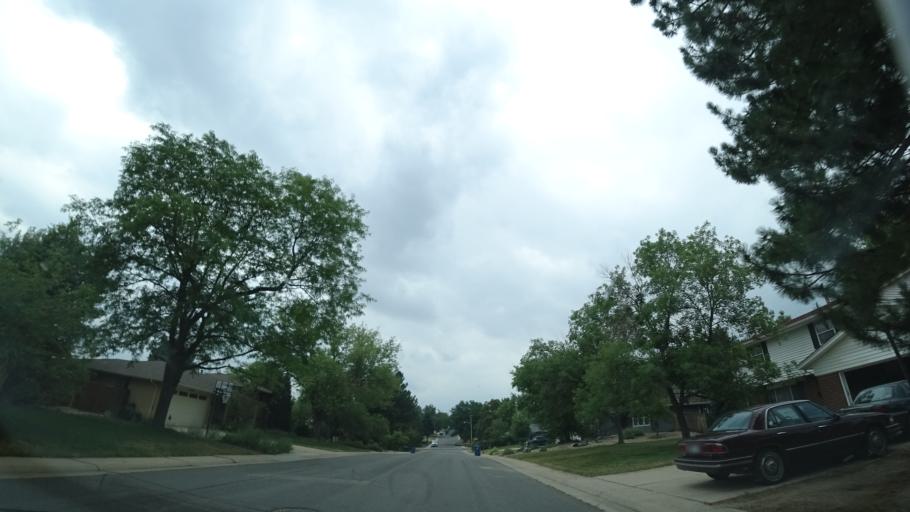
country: US
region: Colorado
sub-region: Jefferson County
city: West Pleasant View
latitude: 39.6991
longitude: -105.1488
